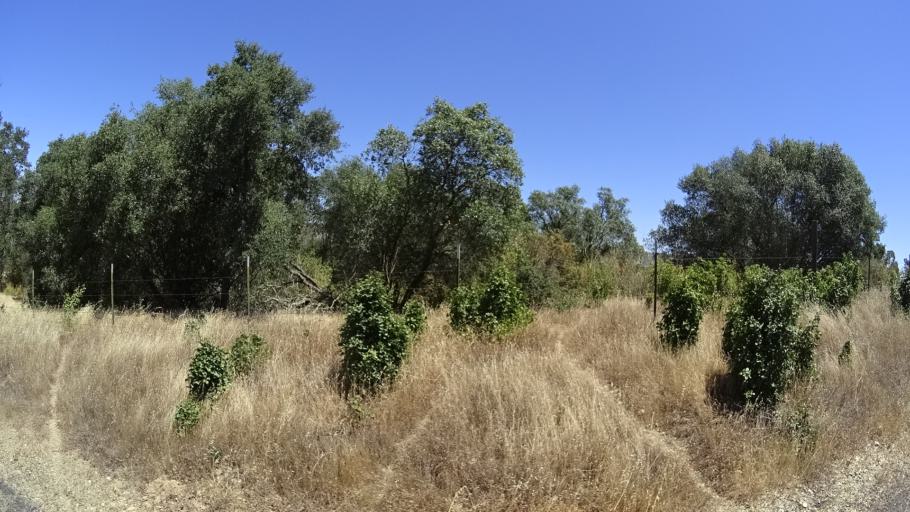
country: US
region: California
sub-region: Calaveras County
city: Copperopolis
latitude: 37.9762
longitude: -120.6866
